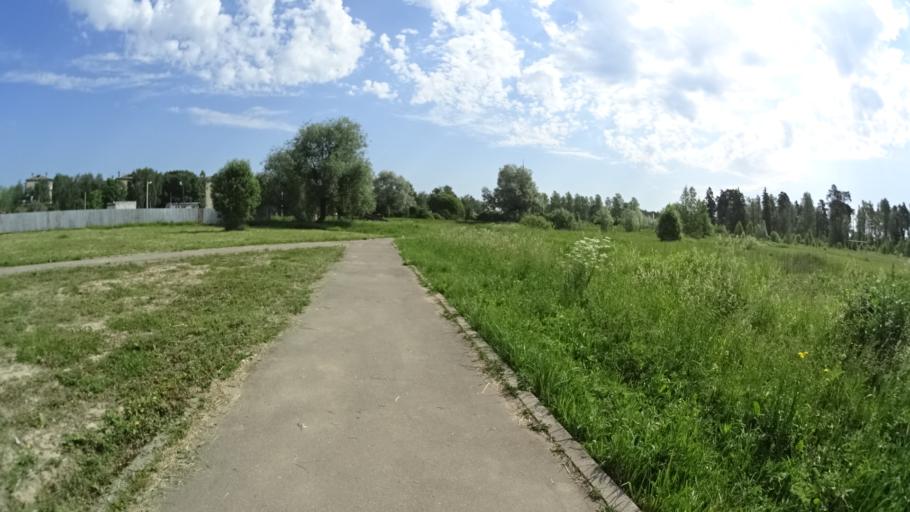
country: RU
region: Moskovskaya
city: Lesnoy
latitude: 56.0757
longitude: 37.9243
